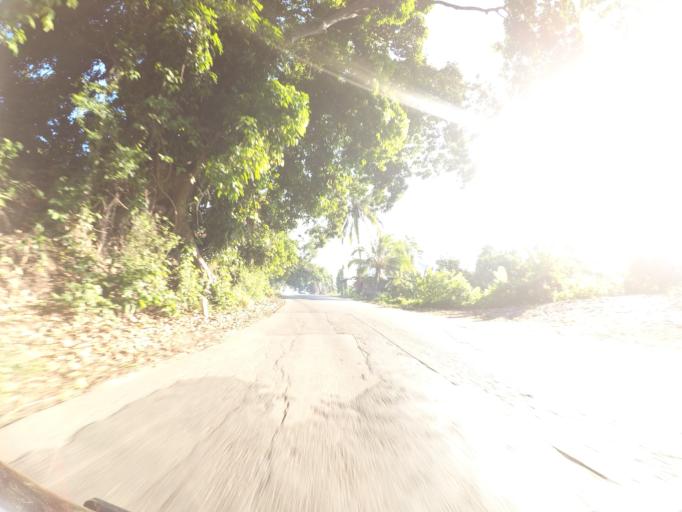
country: TZ
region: Pemba South
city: Chake Chake
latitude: -5.3061
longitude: 39.7496
